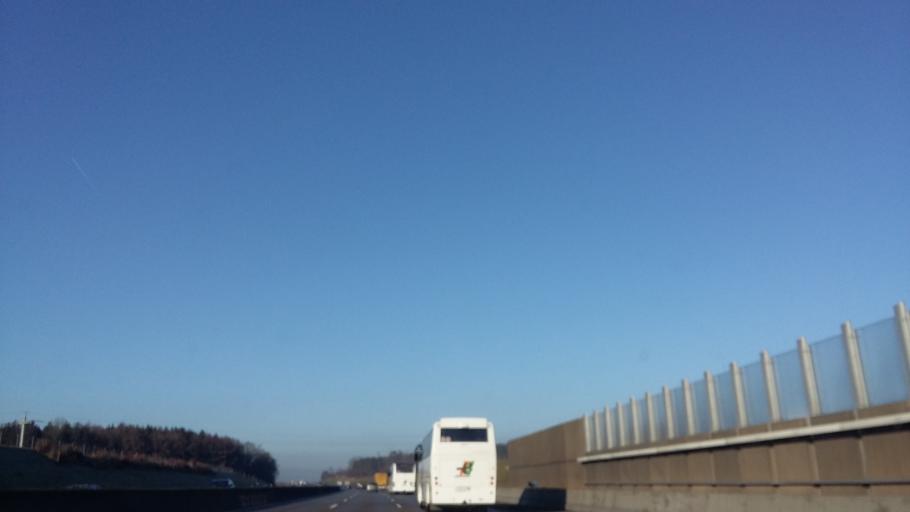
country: DE
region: Bavaria
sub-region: Upper Bavaria
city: Sulzemoos
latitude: 48.2872
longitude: 11.2562
